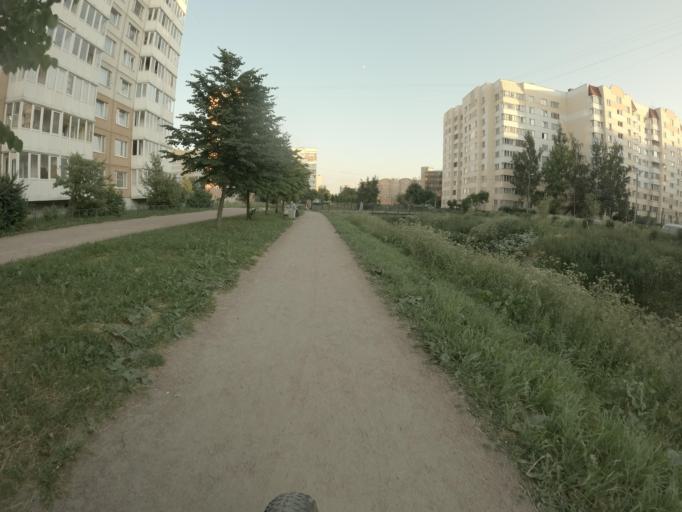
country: RU
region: St.-Petersburg
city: Dachnoye
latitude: 59.8495
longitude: 30.2466
